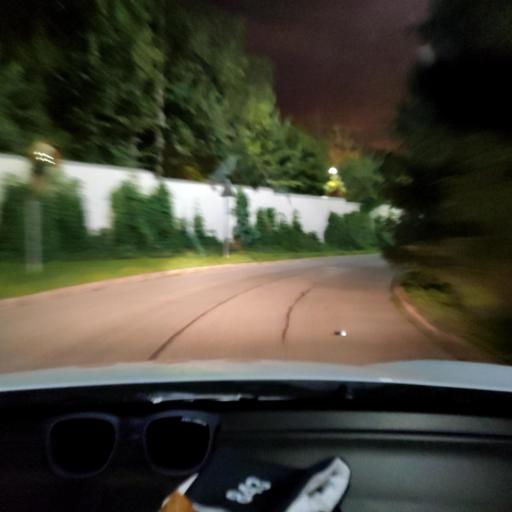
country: RU
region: Tatarstan
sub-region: Gorod Kazan'
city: Kazan
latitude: 55.7426
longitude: 49.1649
